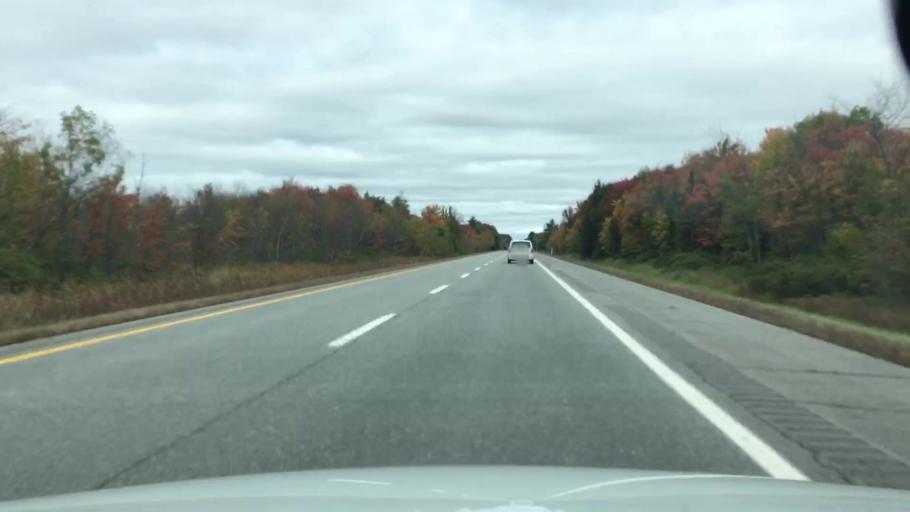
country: US
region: Maine
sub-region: Kennebec County
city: Benton
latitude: 44.6121
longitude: -69.5652
